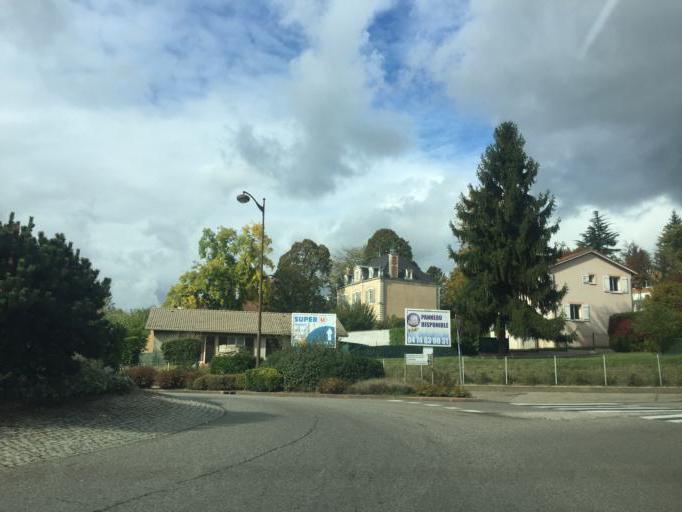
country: FR
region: Rhone-Alpes
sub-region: Departement de l'Ain
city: Montluel
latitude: 45.8512
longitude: 5.0665
